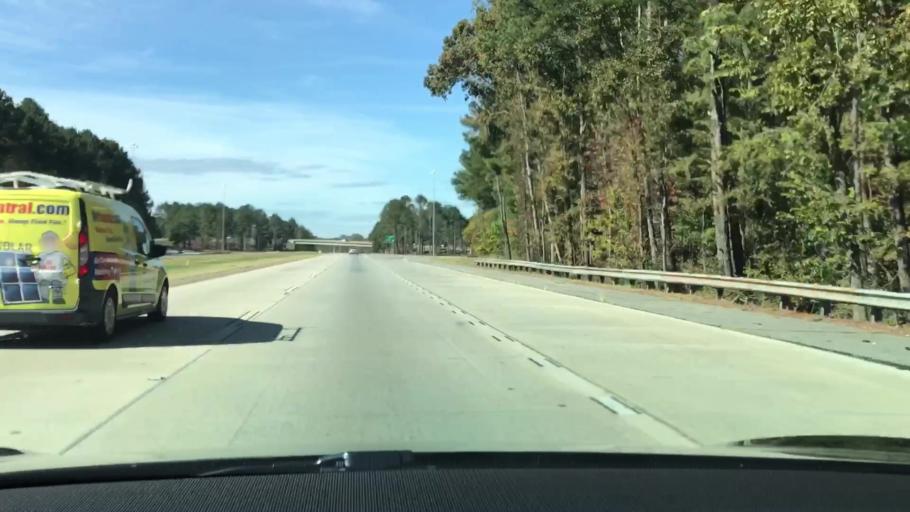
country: US
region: Georgia
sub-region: Greene County
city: Greensboro
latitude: 33.5460
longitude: -83.1987
